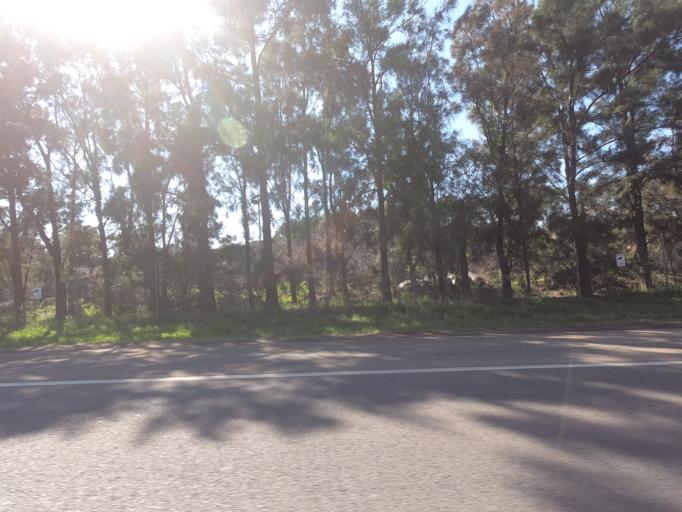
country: AU
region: New South Wales
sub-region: Wollongong
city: Mount Saint Thomas
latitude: -34.4565
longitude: 150.8548
